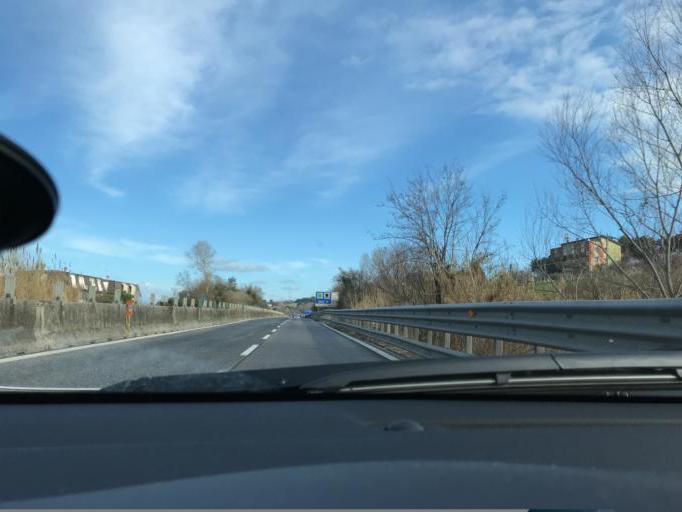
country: IT
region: The Marches
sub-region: Provincia di Ancona
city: Falconara Marittima
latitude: 43.6093
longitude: 13.3743
